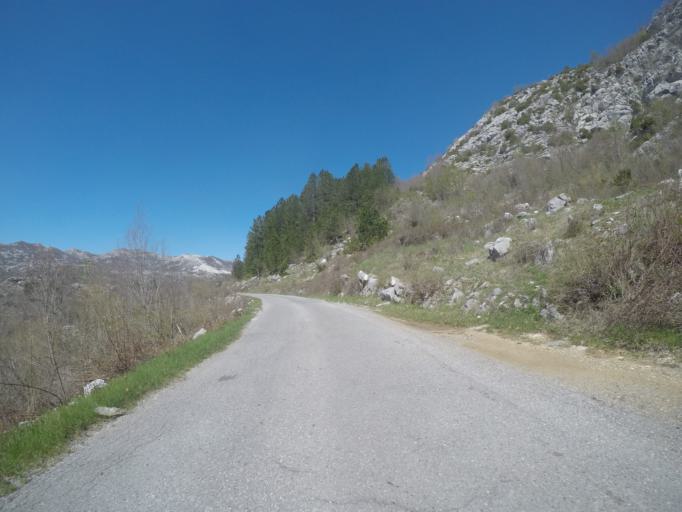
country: ME
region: Cetinje
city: Cetinje
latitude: 42.4601
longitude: 18.8676
